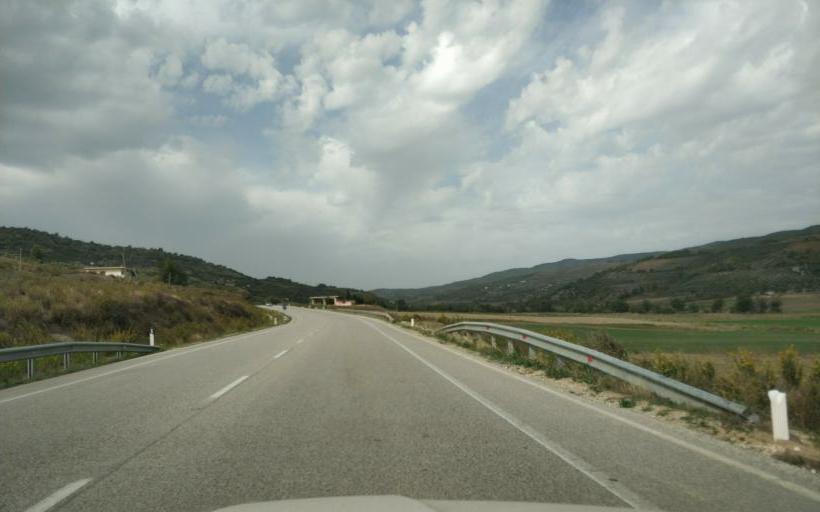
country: AL
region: Gjirokaster
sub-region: Rrethi i Tepelenes
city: Krahes
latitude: 40.4469
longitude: 19.8487
